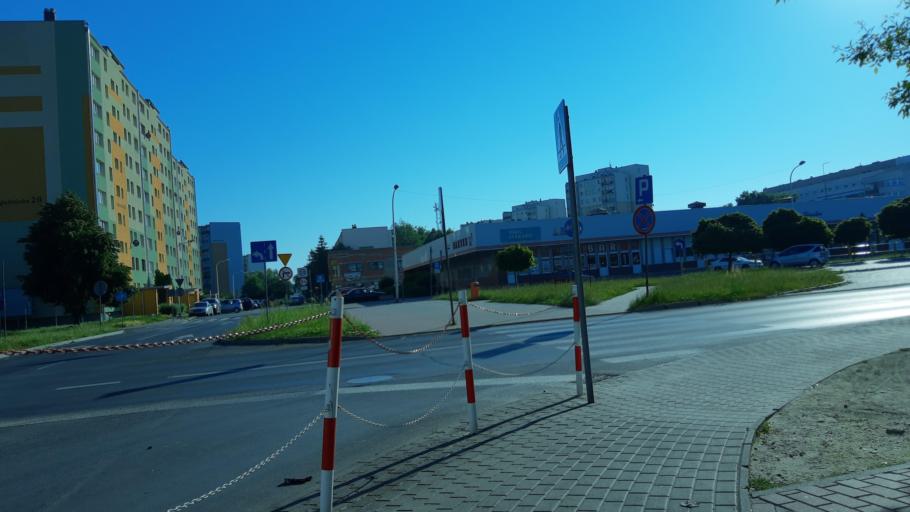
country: PL
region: Lodz Voivodeship
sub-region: Powiat sieradzki
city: Sieradz
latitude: 51.5882
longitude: 18.7197
